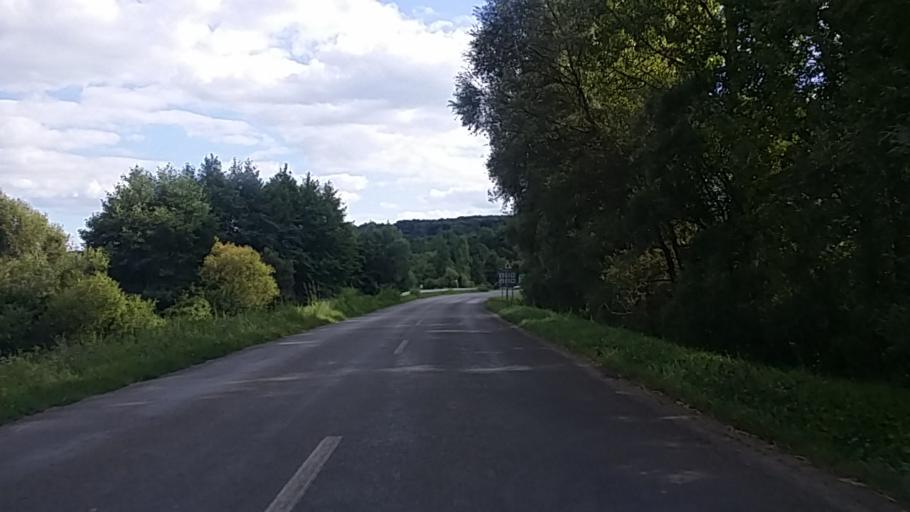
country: HU
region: Baranya
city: Sasd
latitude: 46.2122
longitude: 18.1045
